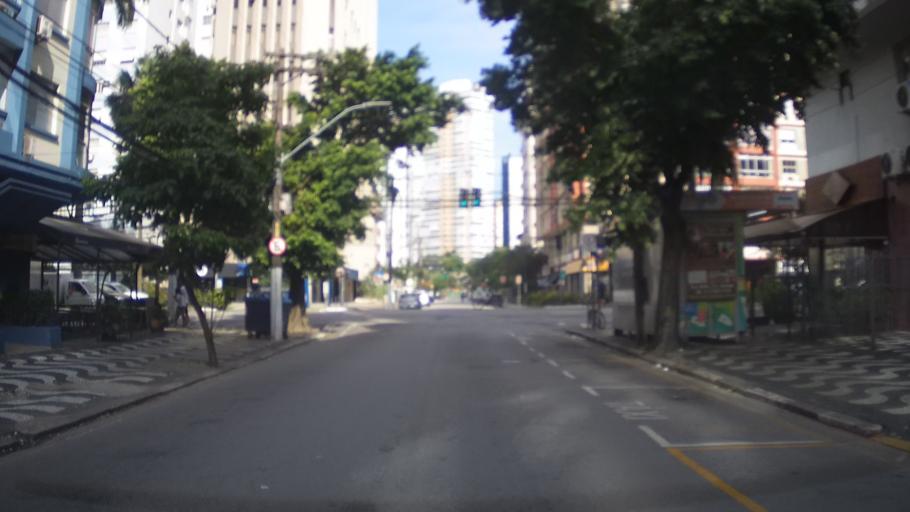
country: BR
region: Sao Paulo
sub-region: Santos
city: Santos
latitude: -23.9646
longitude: -46.3320
